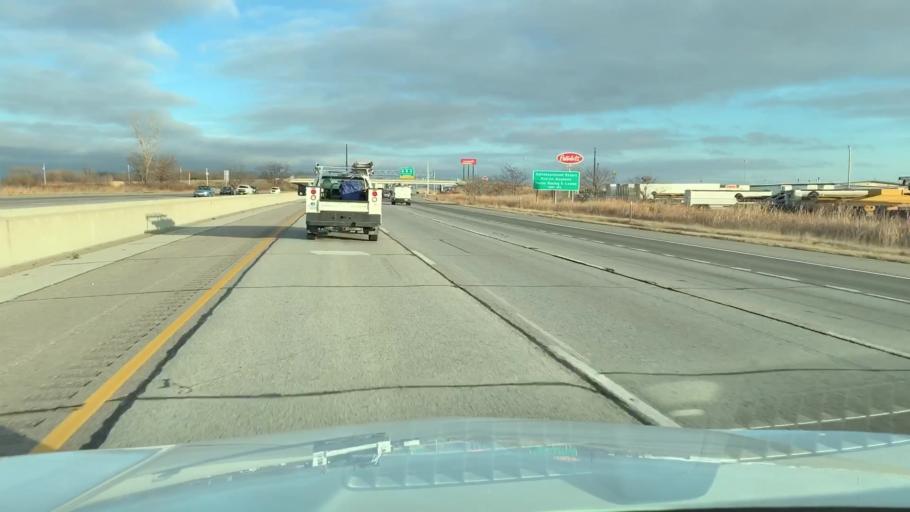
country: US
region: Iowa
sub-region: Polk County
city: Altoona
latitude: 41.6619
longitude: -93.5082
